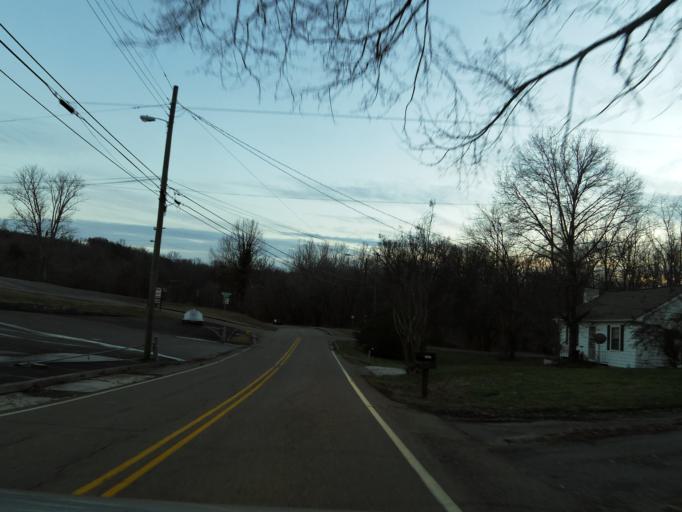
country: US
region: Tennessee
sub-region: Knox County
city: Knoxville
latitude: 35.9430
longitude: -83.8912
